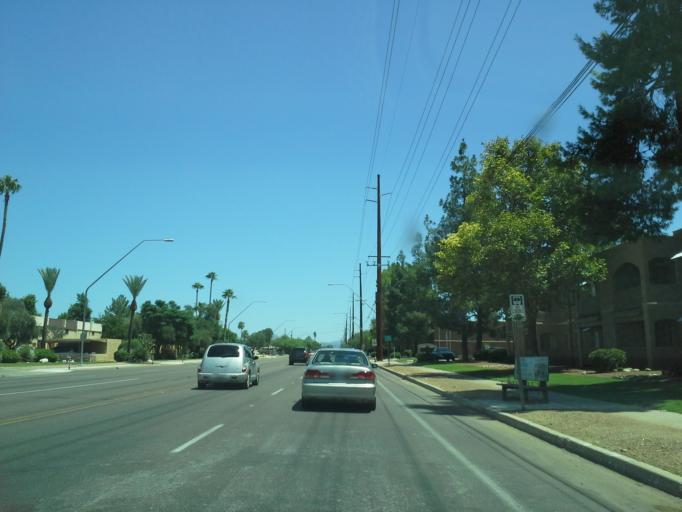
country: US
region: Arizona
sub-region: Pima County
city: Catalina Foothills
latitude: 32.2647
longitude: -110.9522
